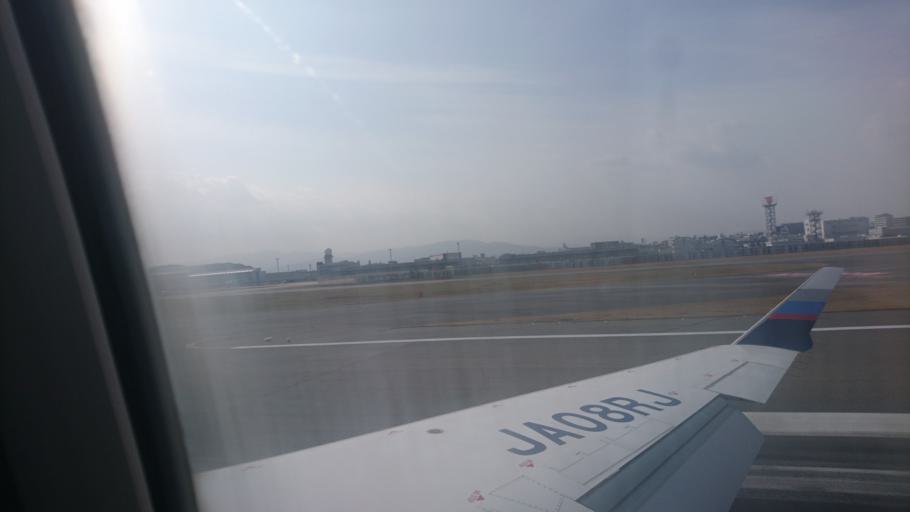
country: JP
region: Fukuoka
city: Fukuoka-shi
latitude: 33.5921
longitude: 130.4465
